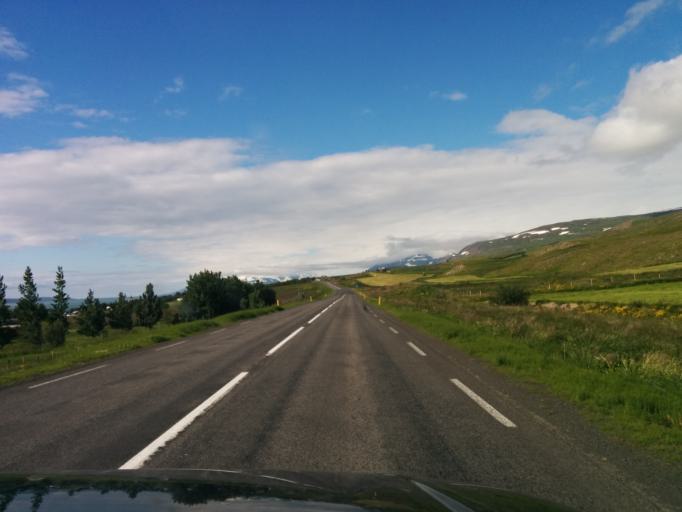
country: IS
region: Northeast
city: Akureyri
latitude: 65.7366
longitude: -18.0739
